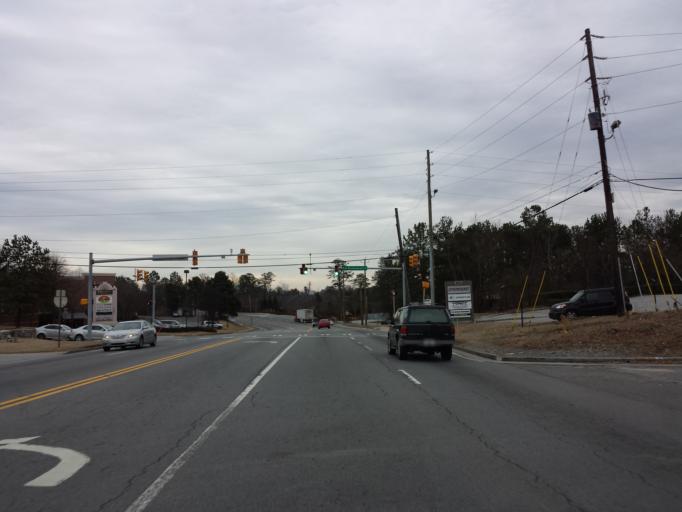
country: US
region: Georgia
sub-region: Cobb County
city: Vinings
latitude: 33.8408
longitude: -84.4852
